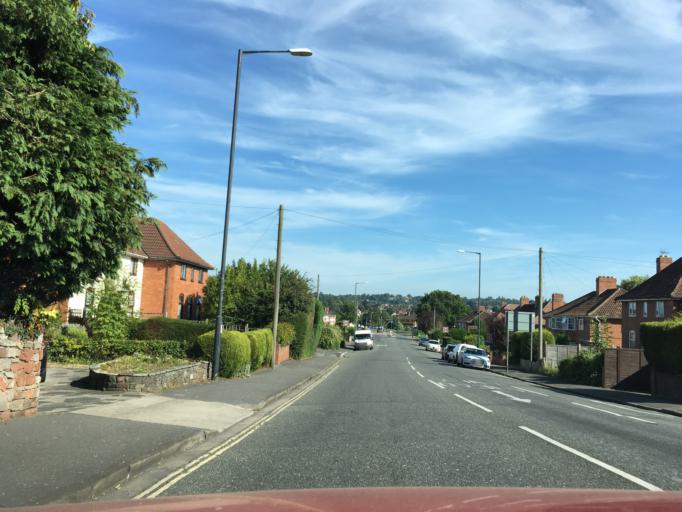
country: GB
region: England
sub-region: North Somerset
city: Easton-in-Gordano
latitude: 51.4891
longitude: -2.6510
